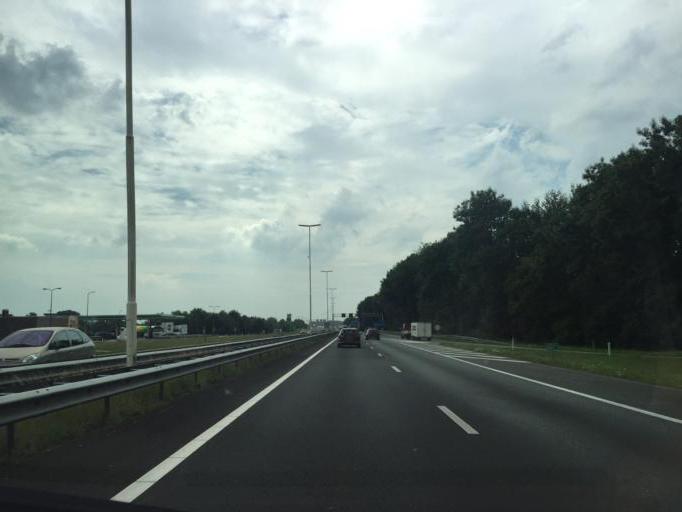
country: NL
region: Utrecht
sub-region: Gemeente De Bilt
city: De Bilt
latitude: 52.1303
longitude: 5.1506
